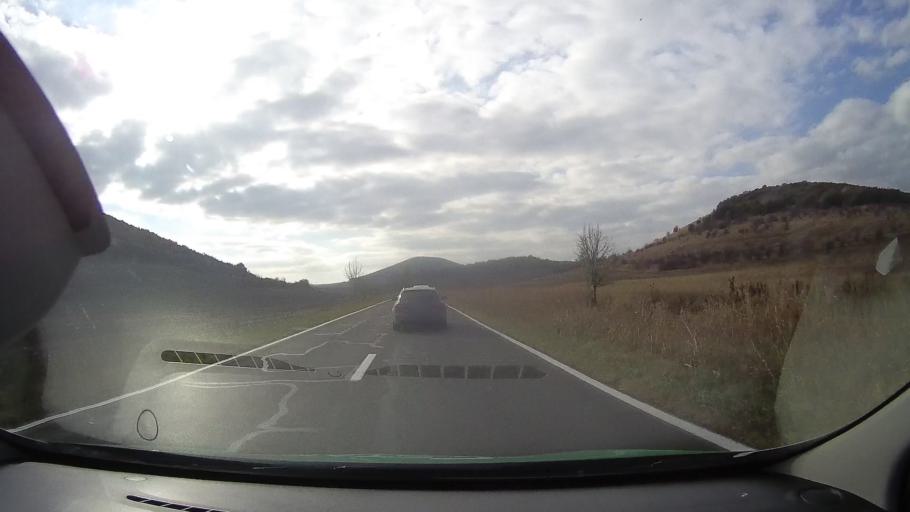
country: RO
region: Tulcea
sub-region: Comuna Ciucurova
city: Ciucurova
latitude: 44.9640
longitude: 28.5258
